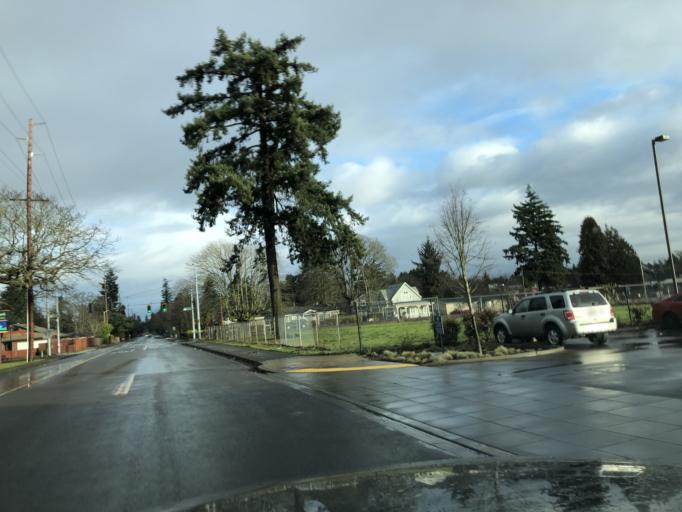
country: US
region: Washington
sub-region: Pierce County
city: Parkland
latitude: 47.1468
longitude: -122.4371
